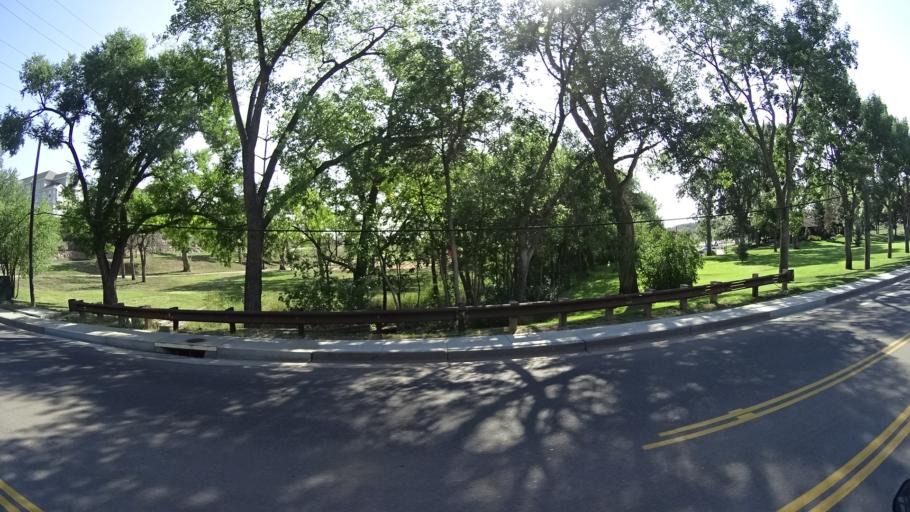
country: US
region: Colorado
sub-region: El Paso County
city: Colorado Springs
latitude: 38.8243
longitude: -104.8593
